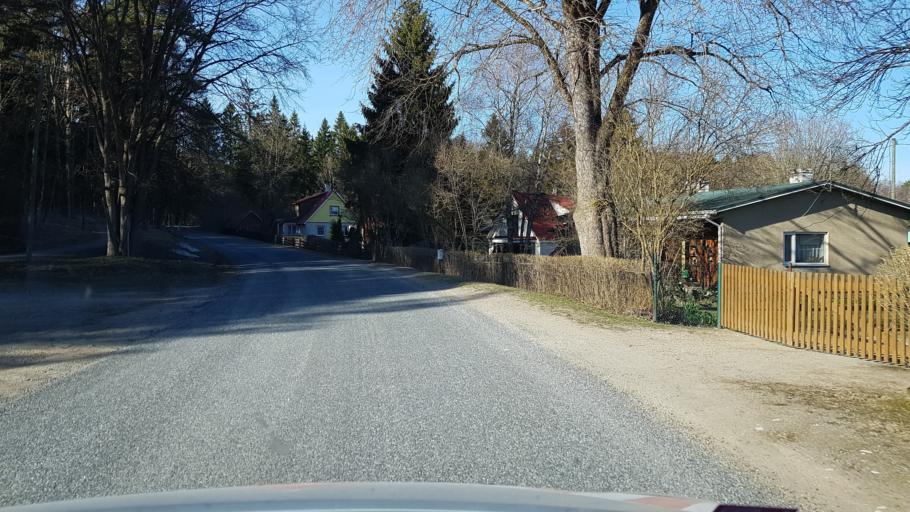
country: EE
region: Laeaene-Virumaa
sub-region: Vinni vald
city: Vinni
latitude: 59.1668
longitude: 26.5919
